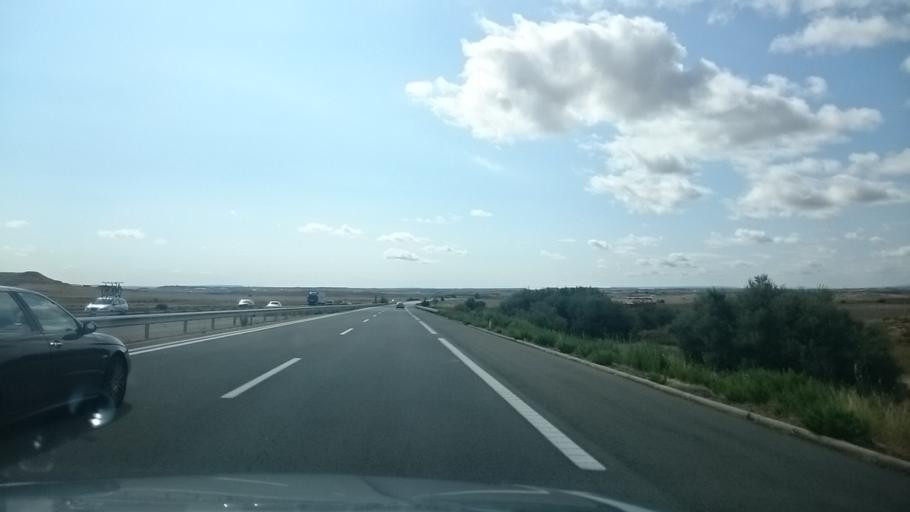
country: ES
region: La Rioja
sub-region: Provincia de La Rioja
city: Rincon de Soto
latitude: 42.2036
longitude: -1.8607
